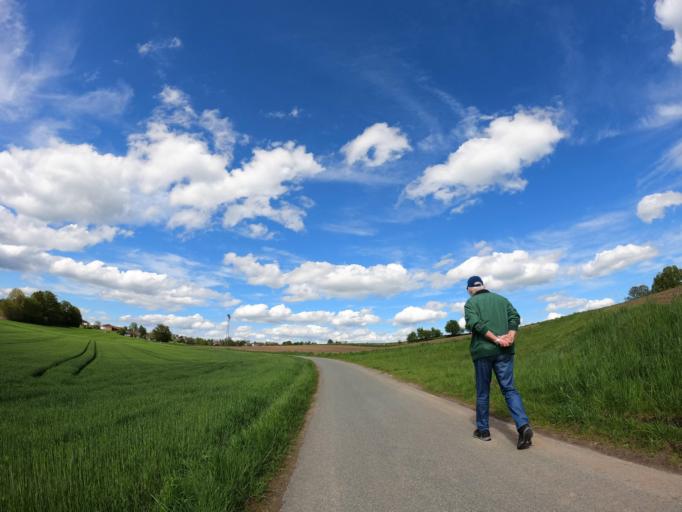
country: DE
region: Bavaria
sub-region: Upper Bavaria
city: Ebersberg
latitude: 48.0651
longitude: 11.9543
